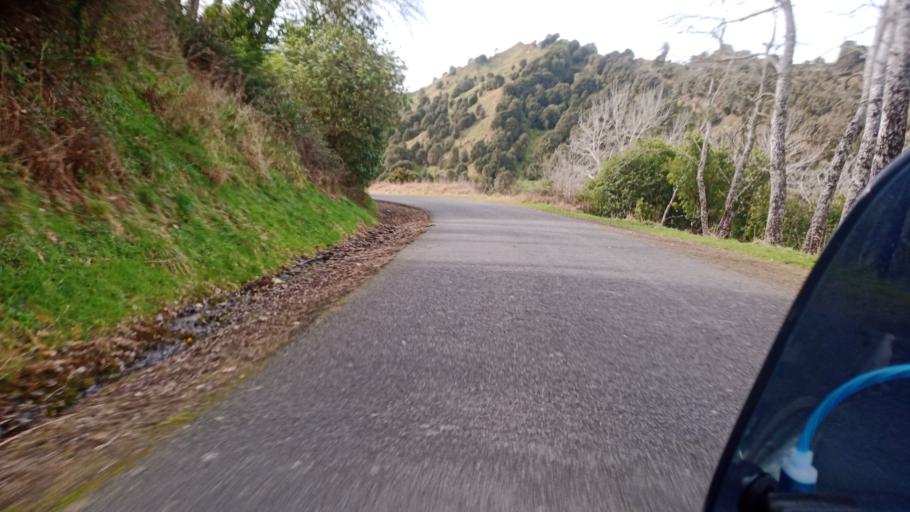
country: NZ
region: Hawke's Bay
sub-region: Wairoa District
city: Wairoa
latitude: -38.7970
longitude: 177.4474
